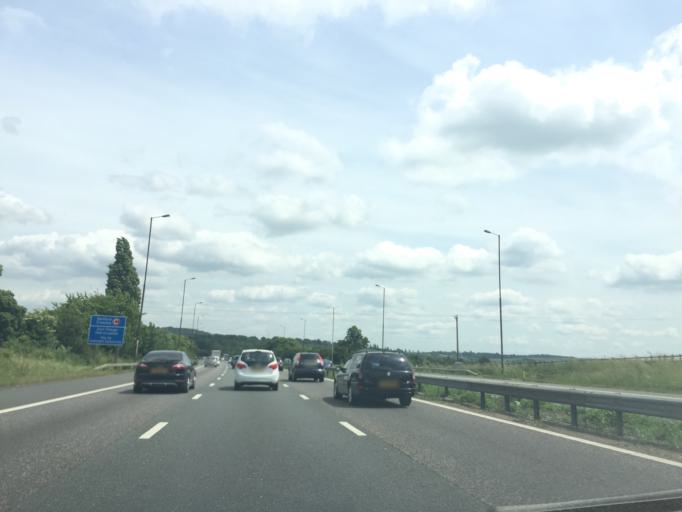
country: GB
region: England
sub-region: Kent
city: Dartford
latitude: 51.4265
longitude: 0.2212
